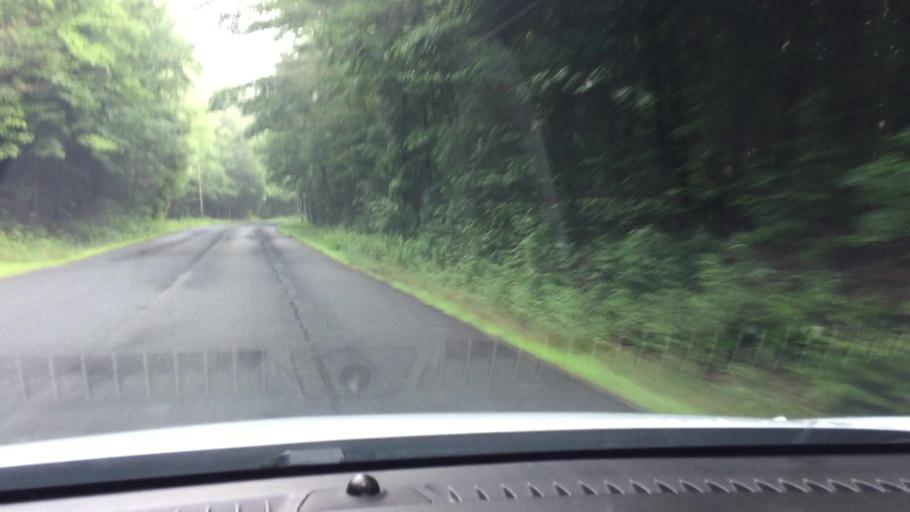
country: US
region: Massachusetts
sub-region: Hampshire County
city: Chesterfield
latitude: 42.2982
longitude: -72.9059
